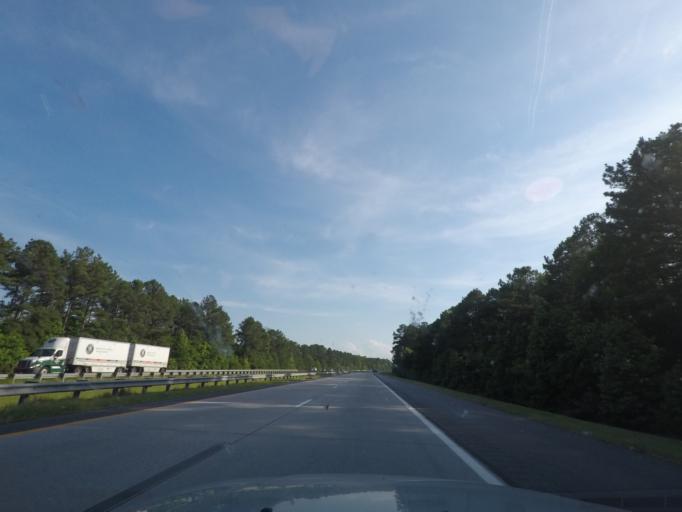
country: US
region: North Carolina
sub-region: Granville County
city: Oxford
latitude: 36.2548
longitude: -78.6205
